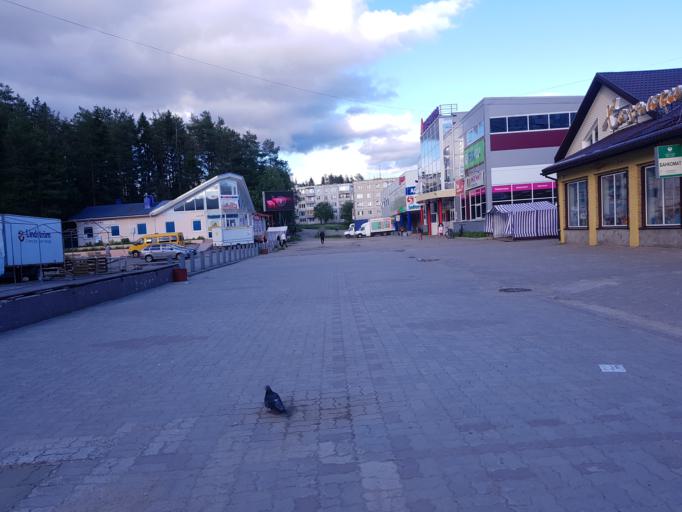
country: RU
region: Republic of Karelia
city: Kostomuksha
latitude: 64.5885
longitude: 30.6010
